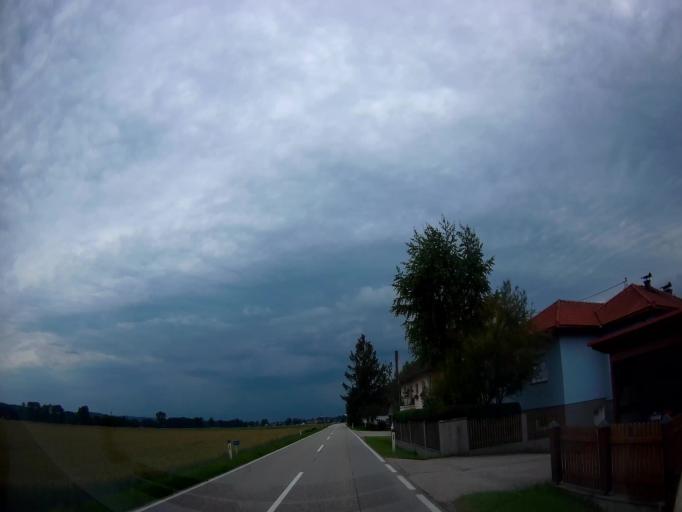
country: AT
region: Upper Austria
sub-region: Politischer Bezirk Braunau am Inn
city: Braunau am Inn
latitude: 48.1769
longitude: 13.1281
